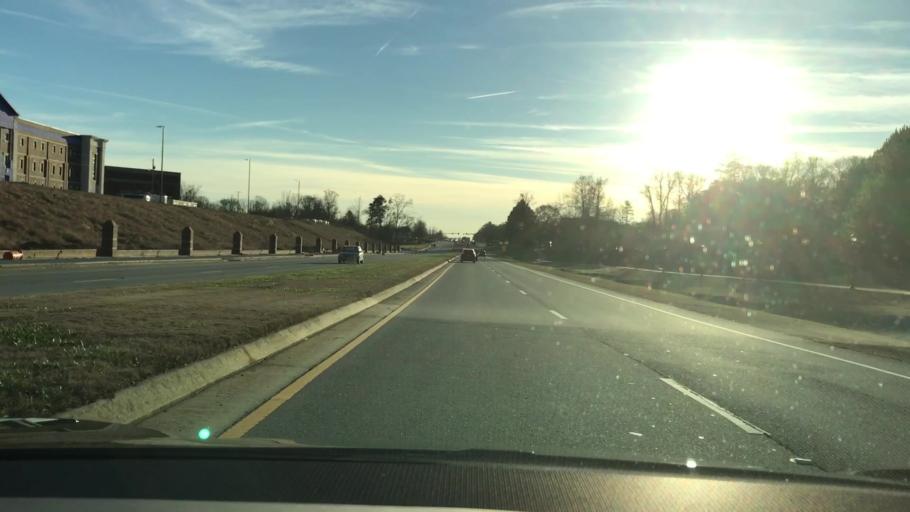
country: US
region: Georgia
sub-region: Gwinnett County
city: Buford
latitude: 34.1196
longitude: -83.9900
